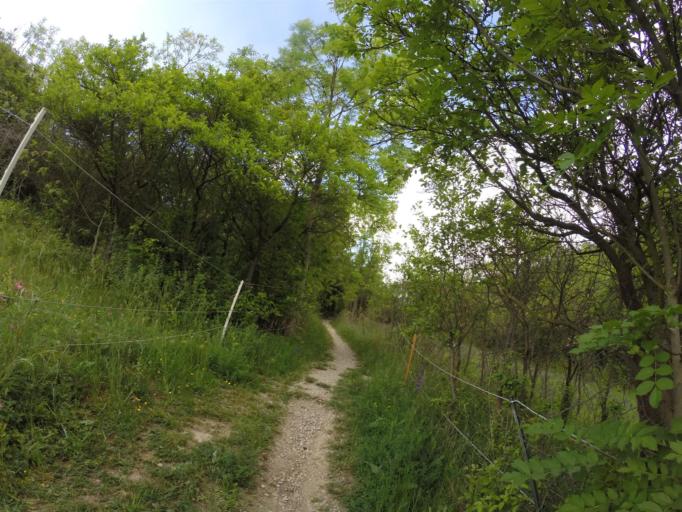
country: DE
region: Thuringia
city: Jena
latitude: 50.9211
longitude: 11.6299
